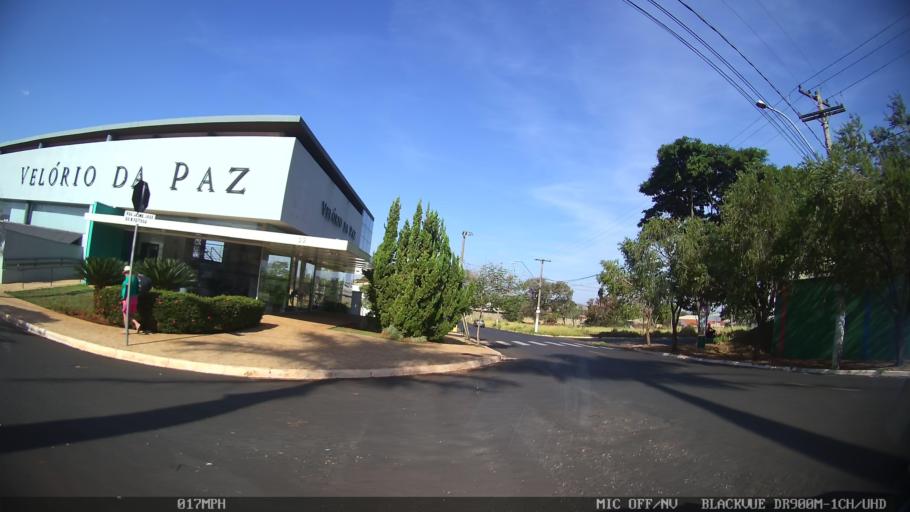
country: BR
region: Sao Paulo
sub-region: Ribeirao Preto
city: Ribeirao Preto
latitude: -21.1784
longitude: -47.7630
